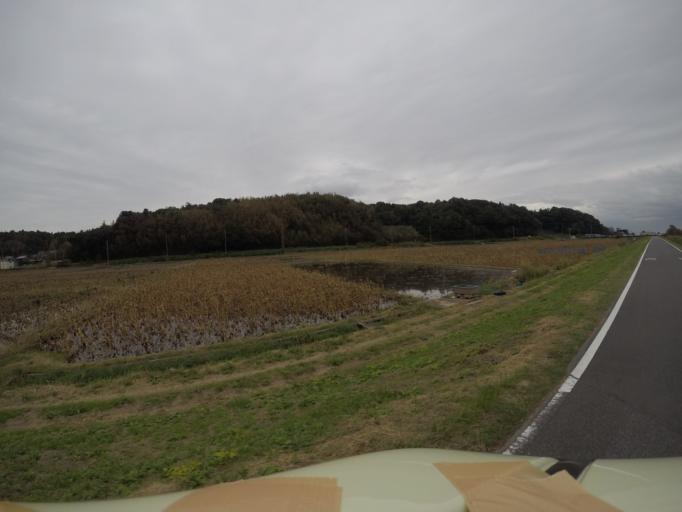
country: JP
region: Ibaraki
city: Ami
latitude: 36.0640
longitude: 140.2863
